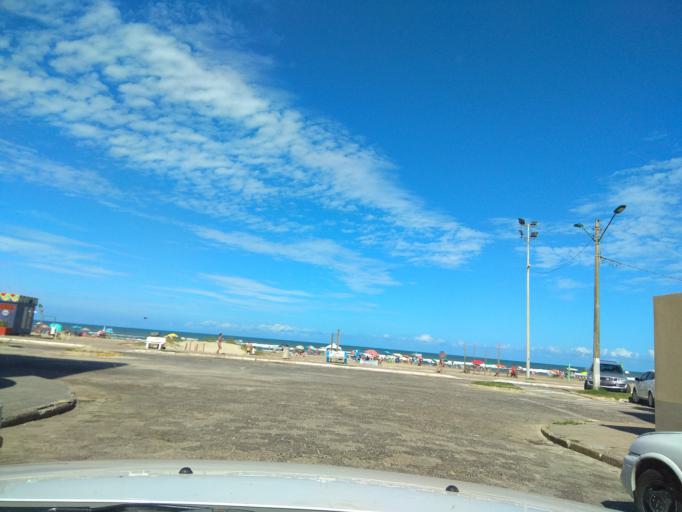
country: BR
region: Santa Catarina
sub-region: Laguna
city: Laguna
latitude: -28.4832
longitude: -48.7669
